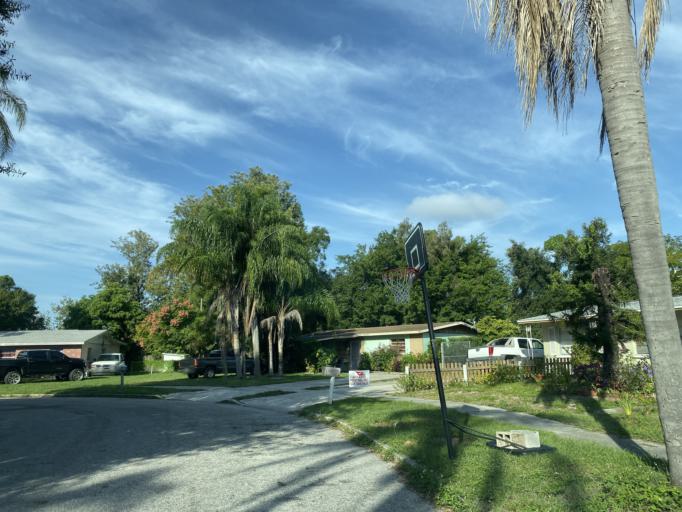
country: US
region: Florida
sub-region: Manatee County
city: Samoset
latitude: 27.4929
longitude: -82.5447
